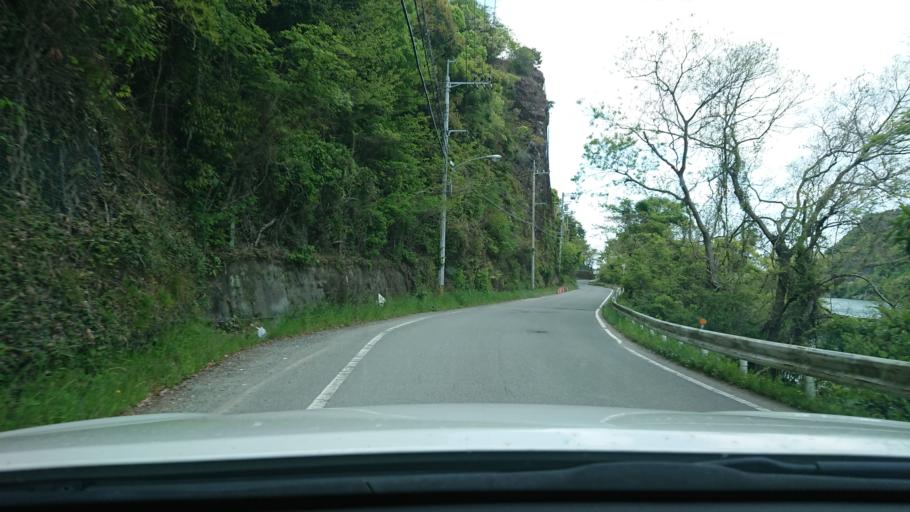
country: JP
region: Tokushima
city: Komatsushimacho
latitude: 33.9845
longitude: 134.5442
